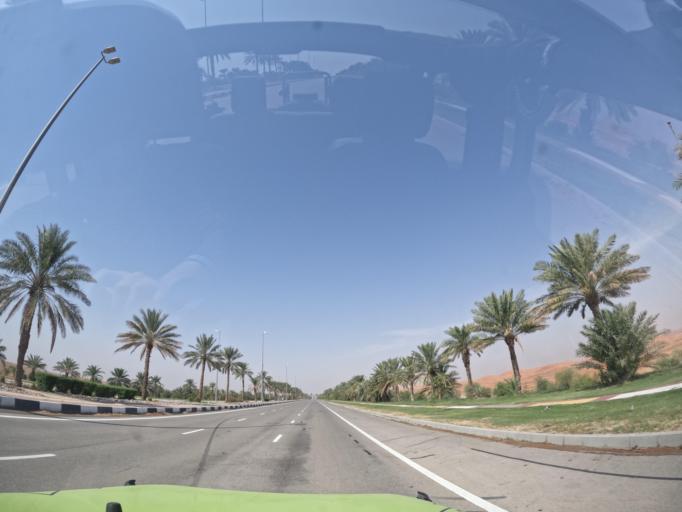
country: AE
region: Abu Dhabi
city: Al Ain
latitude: 24.2618
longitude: 55.6610
